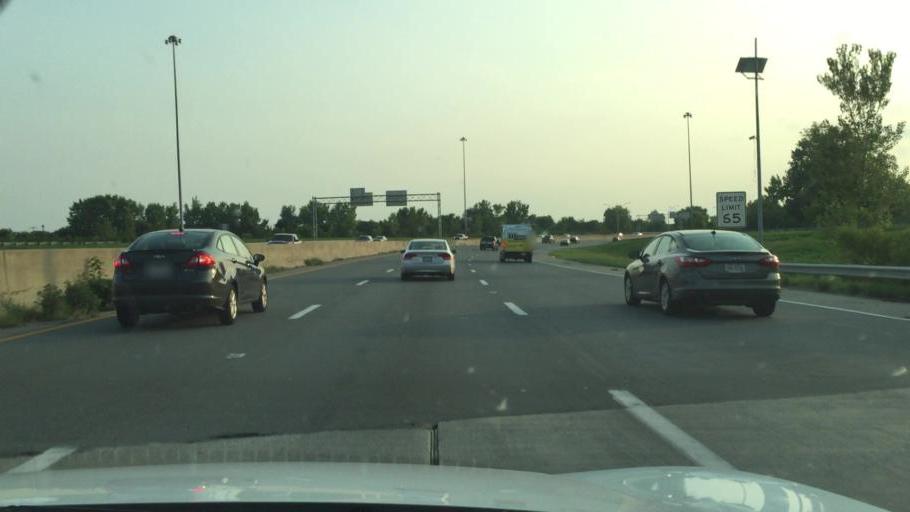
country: US
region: Ohio
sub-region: Franklin County
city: Grandview Heights
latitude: 39.9663
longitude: -83.0262
